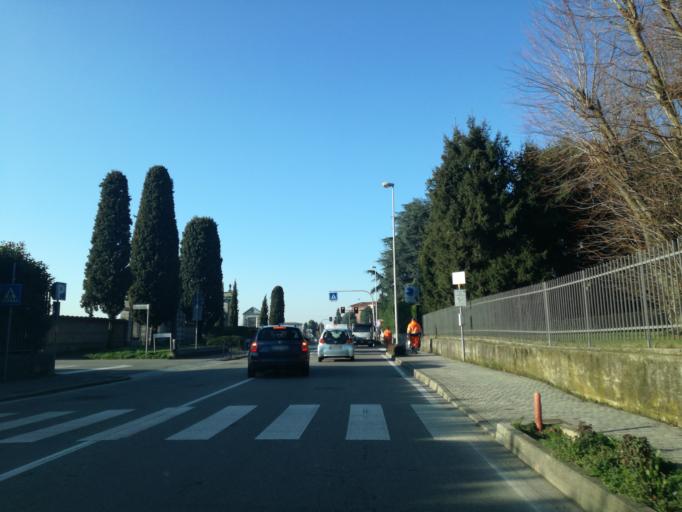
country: IT
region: Lombardy
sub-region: Provincia di Monza e Brianza
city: Bernareggio
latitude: 45.6455
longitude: 9.4043
